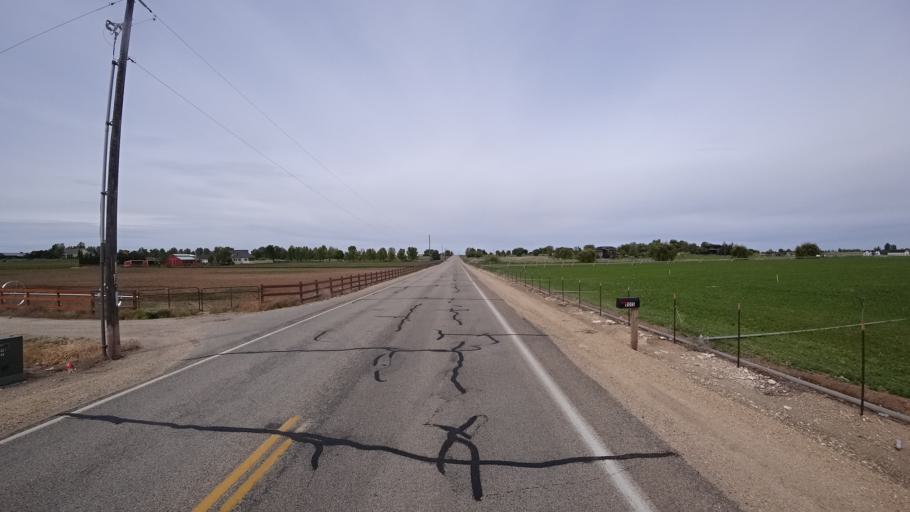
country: US
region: Idaho
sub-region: Ada County
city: Meridian
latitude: 43.5612
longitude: -116.4188
